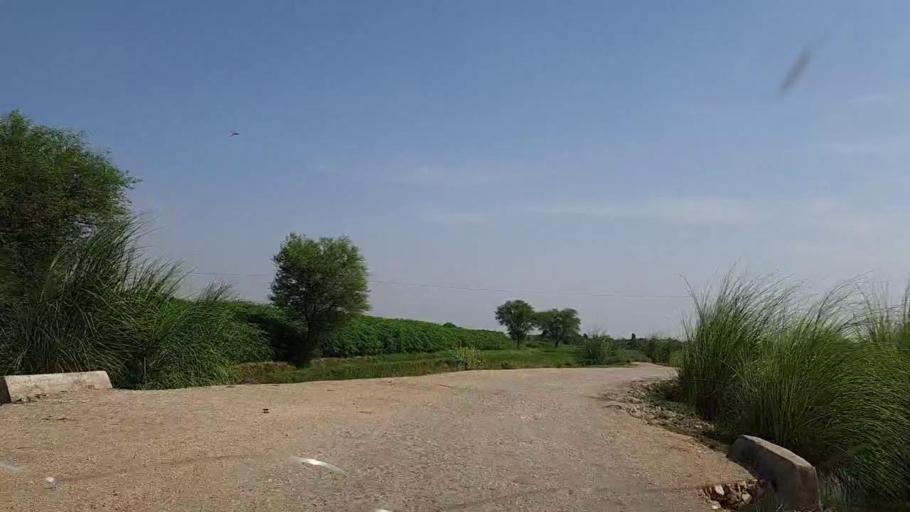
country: PK
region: Sindh
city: Khanpur
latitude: 27.7155
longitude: 69.3623
